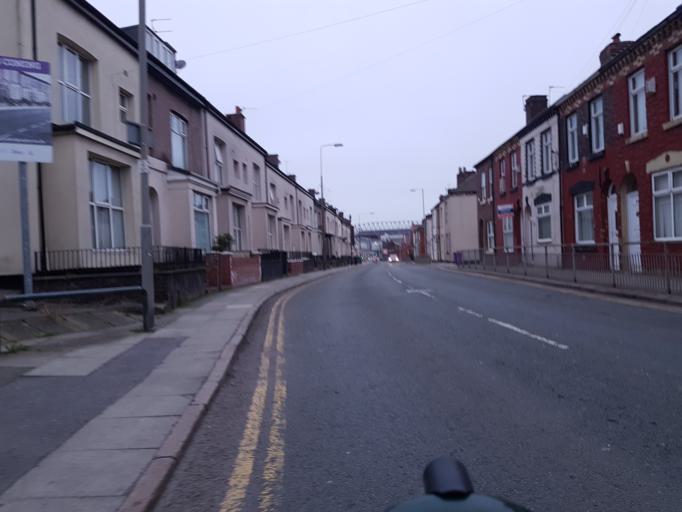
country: GB
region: England
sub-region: Liverpool
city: Liverpool
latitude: 53.4249
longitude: -2.9553
